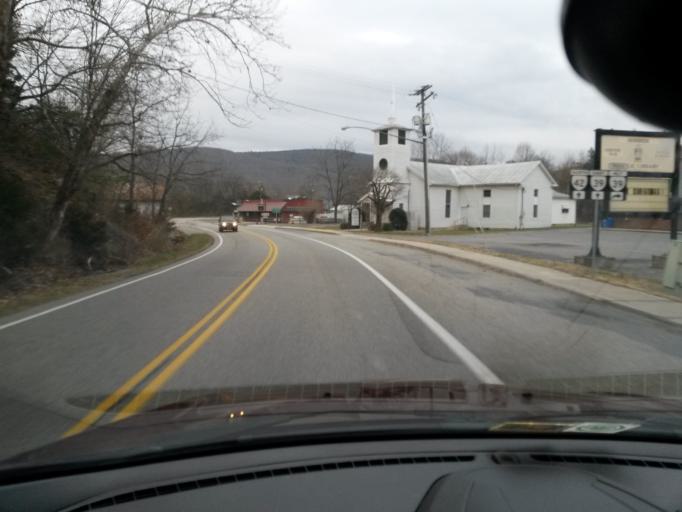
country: US
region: Virginia
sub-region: Rockbridge County
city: East Lexington
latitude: 37.9892
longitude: -79.4987
